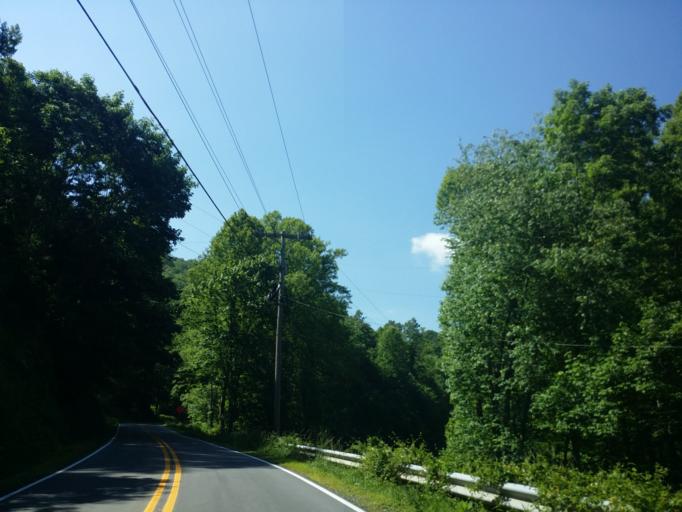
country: US
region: North Carolina
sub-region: Madison County
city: Marshall
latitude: 35.7291
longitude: -82.8414
